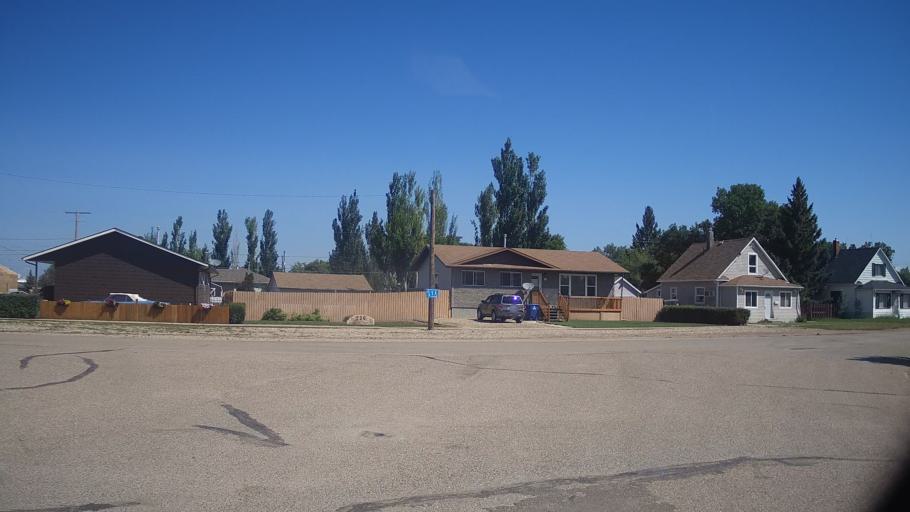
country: CA
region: Saskatchewan
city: Saskatoon
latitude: 51.8963
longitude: -106.0541
